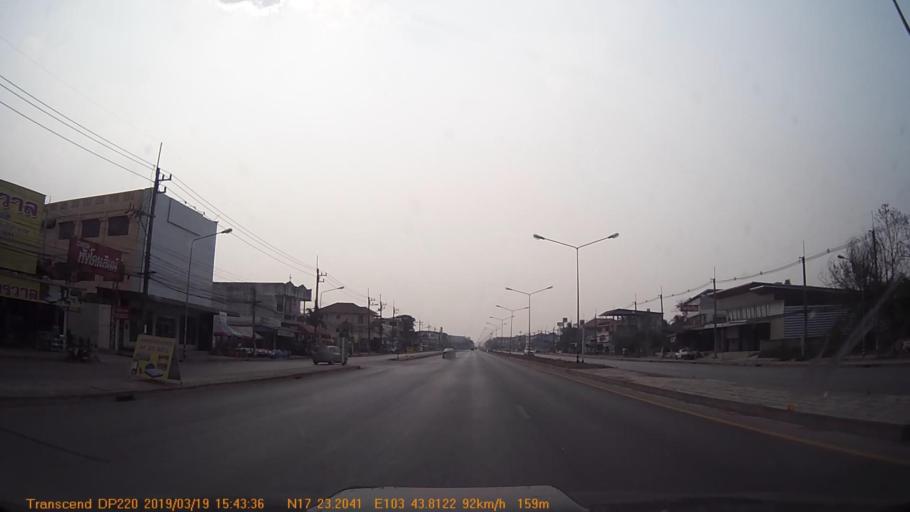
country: TH
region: Sakon Nakhon
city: Phang Khon
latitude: 17.3868
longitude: 103.7299
